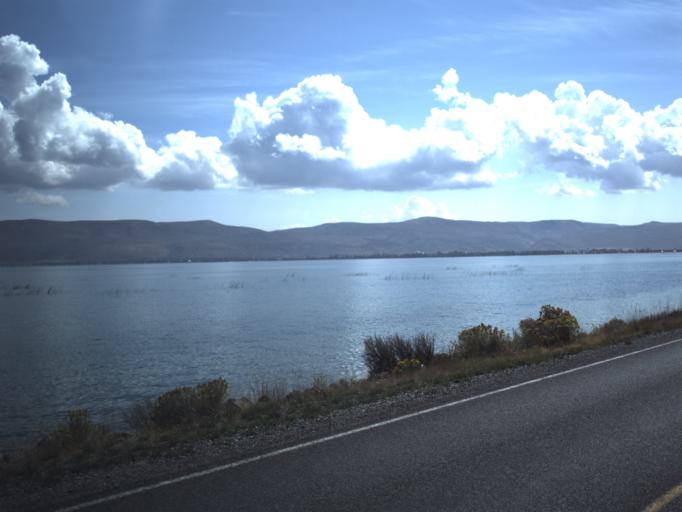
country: US
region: Utah
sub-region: Rich County
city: Randolph
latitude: 41.8774
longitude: -111.3654
